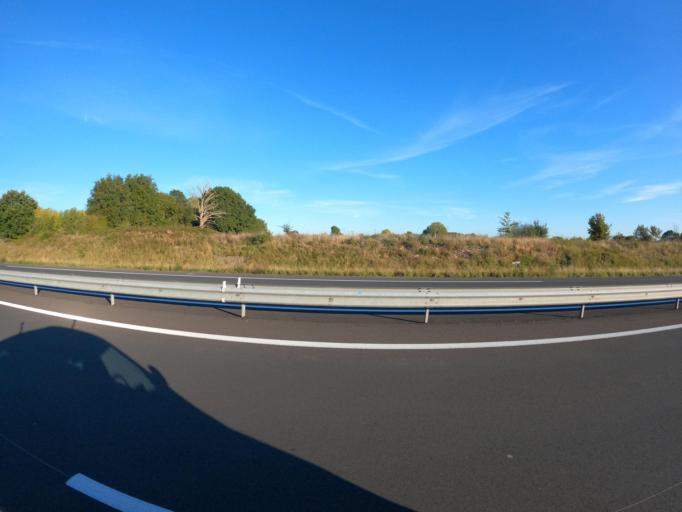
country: FR
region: Pays de la Loire
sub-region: Departement de la Vendee
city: Saint-Fulgent
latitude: 46.8428
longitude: -1.1509
